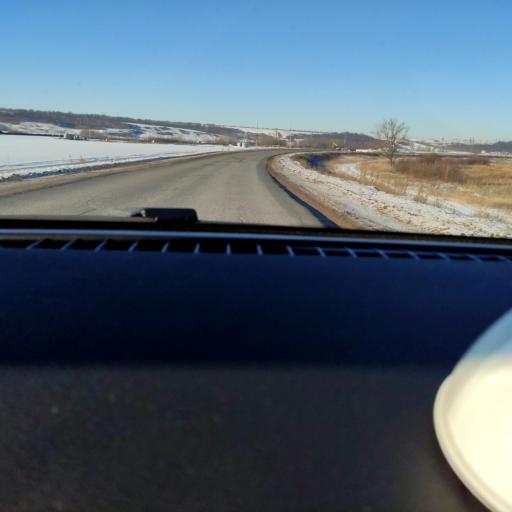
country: RU
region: Samara
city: Spiridonovka
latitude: 53.1357
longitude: 50.6055
